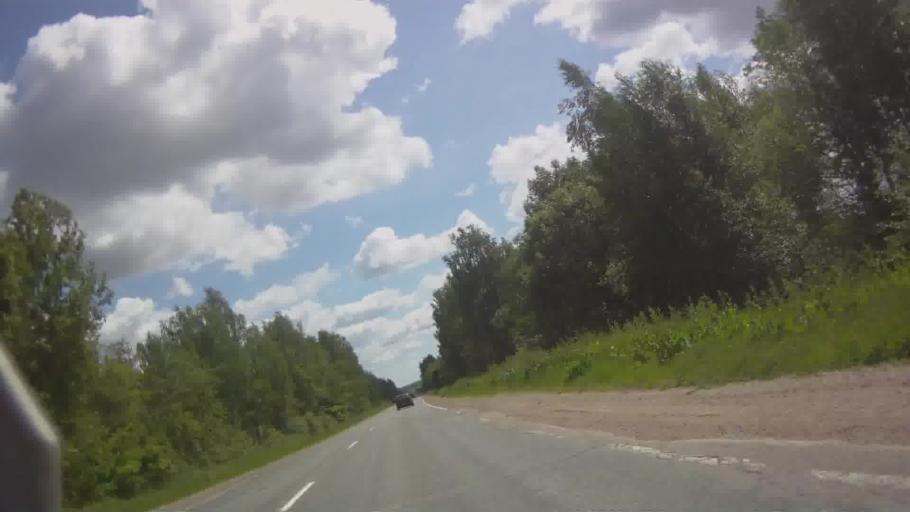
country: LV
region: Varaklani
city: Varaklani
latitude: 56.6081
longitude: 26.8443
